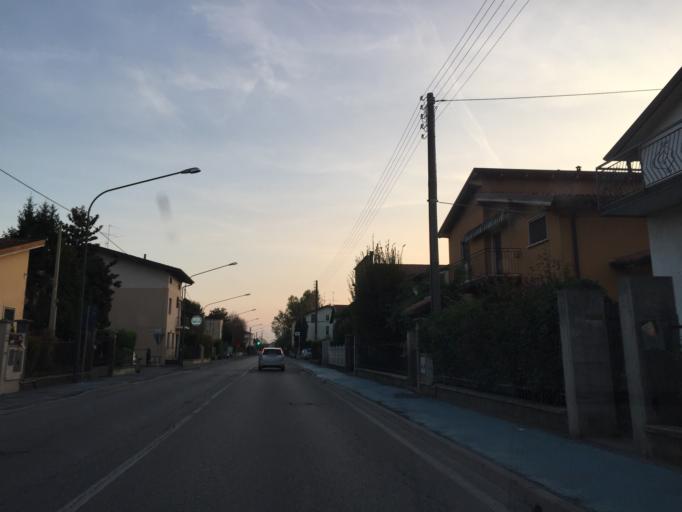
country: IT
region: Lombardy
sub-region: Provincia di Brescia
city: Flero
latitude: 45.4867
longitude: 10.1803
